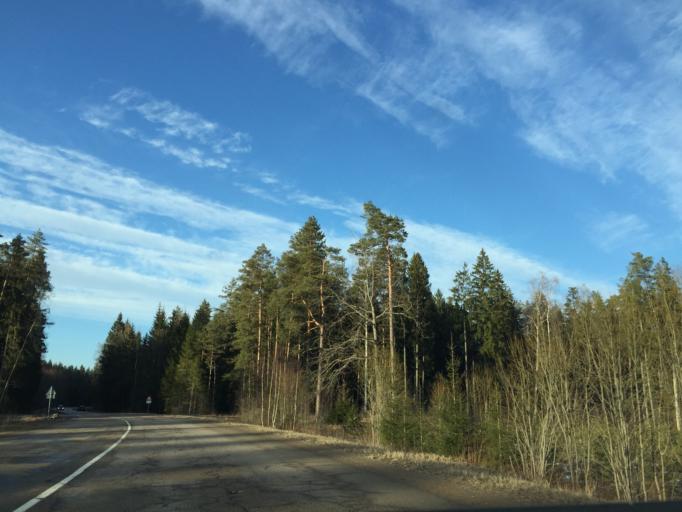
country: LV
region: Kekava
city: Balozi
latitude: 56.7572
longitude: 24.1101
